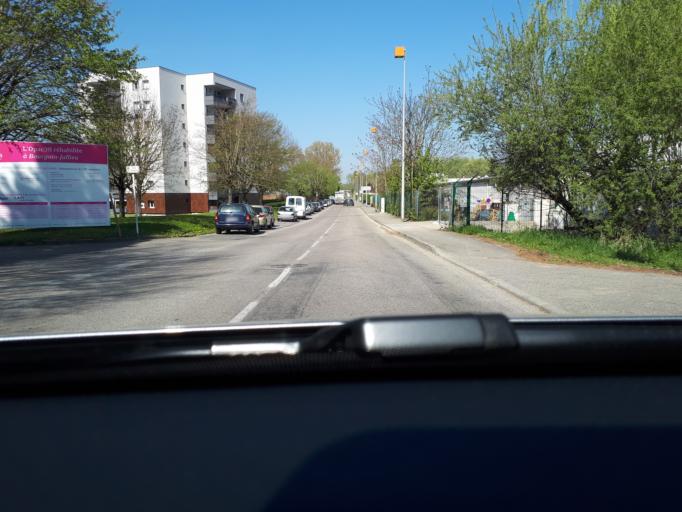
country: FR
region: Rhone-Alpes
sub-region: Departement de l'Isere
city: Bourgoin-Jallieu
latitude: 45.6112
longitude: 5.2732
